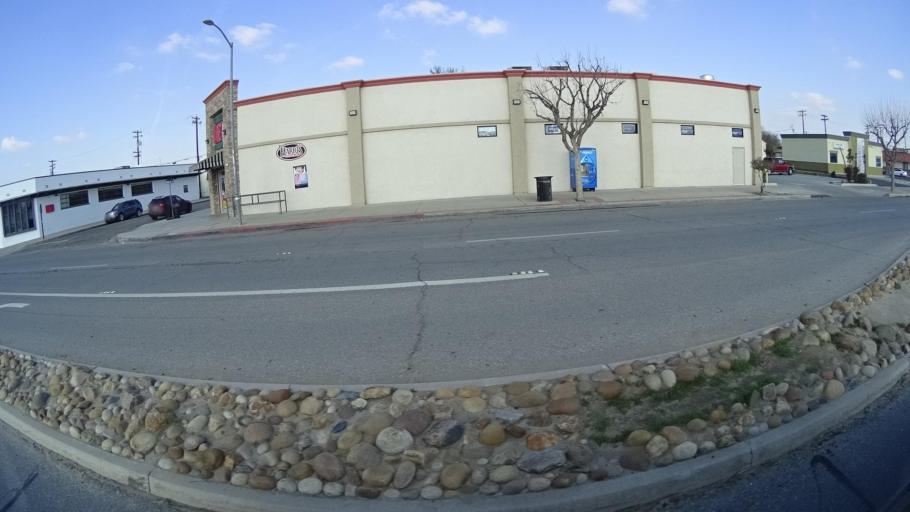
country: US
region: California
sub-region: Kern County
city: Arvin
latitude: 35.2090
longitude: -118.8296
